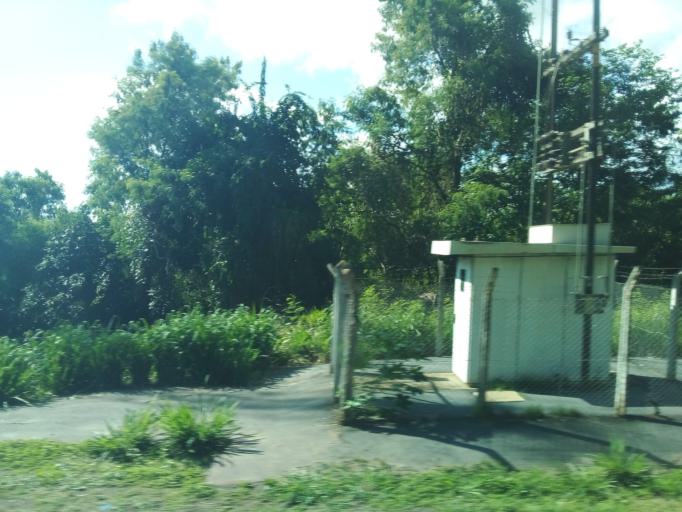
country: BR
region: Minas Gerais
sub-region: Governador Valadares
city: Governador Valadares
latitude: -18.8737
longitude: -41.7820
